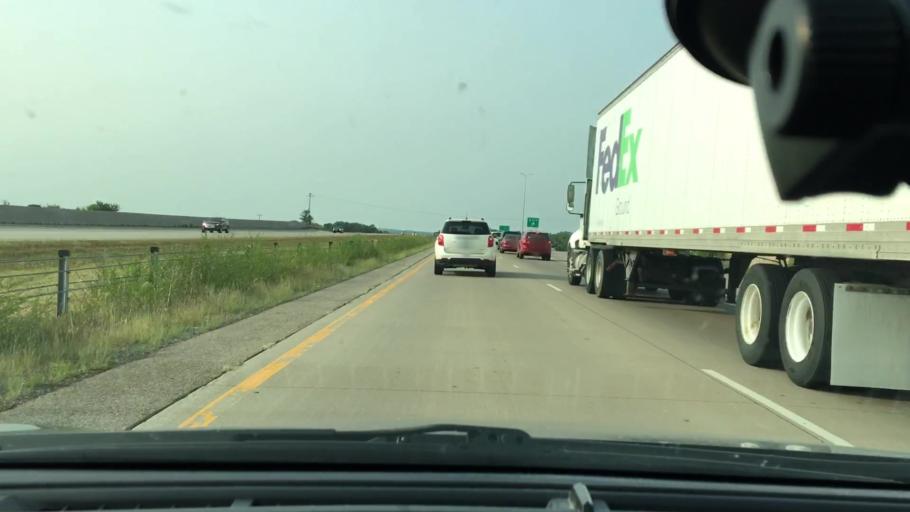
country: US
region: Minnesota
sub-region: Wright County
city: Otsego
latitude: 45.2592
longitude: -93.5554
